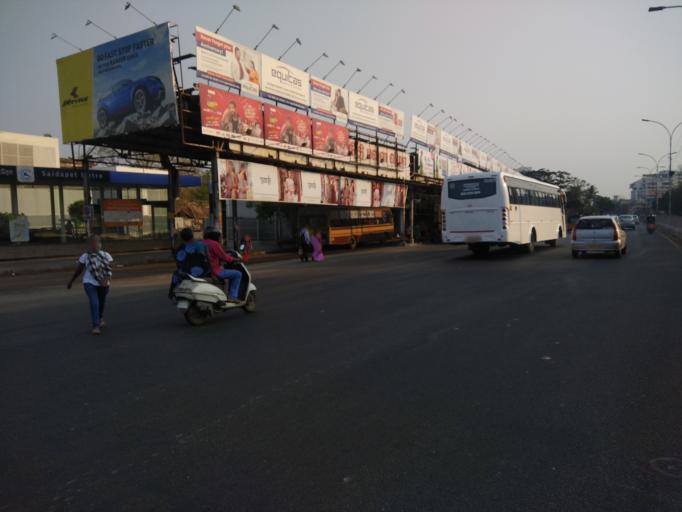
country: IN
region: Tamil Nadu
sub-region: Kancheepuram
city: Alandur
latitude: 13.0236
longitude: 80.2276
